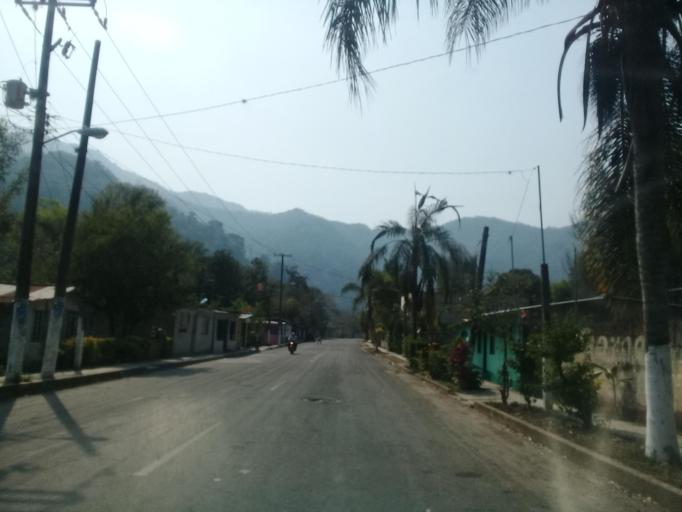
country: MX
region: Veracruz
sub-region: Ixtaczoquitlan
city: Campo Chico
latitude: 18.8340
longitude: -97.0244
